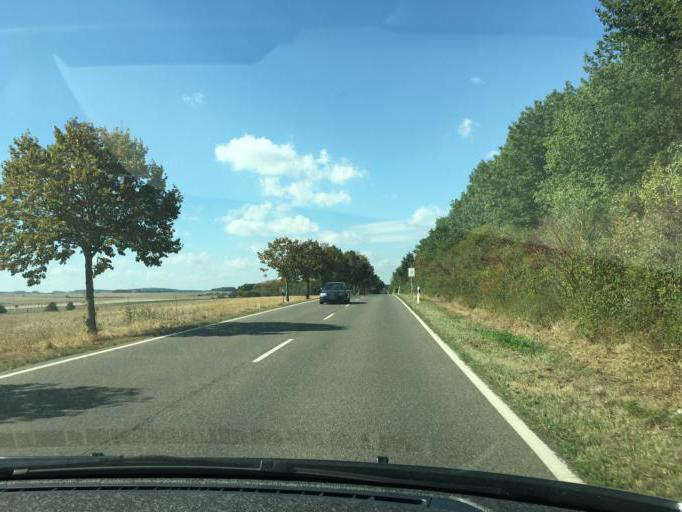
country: DE
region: North Rhine-Westphalia
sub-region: Regierungsbezirk Koln
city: Vettweiss
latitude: 50.6704
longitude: 6.5940
